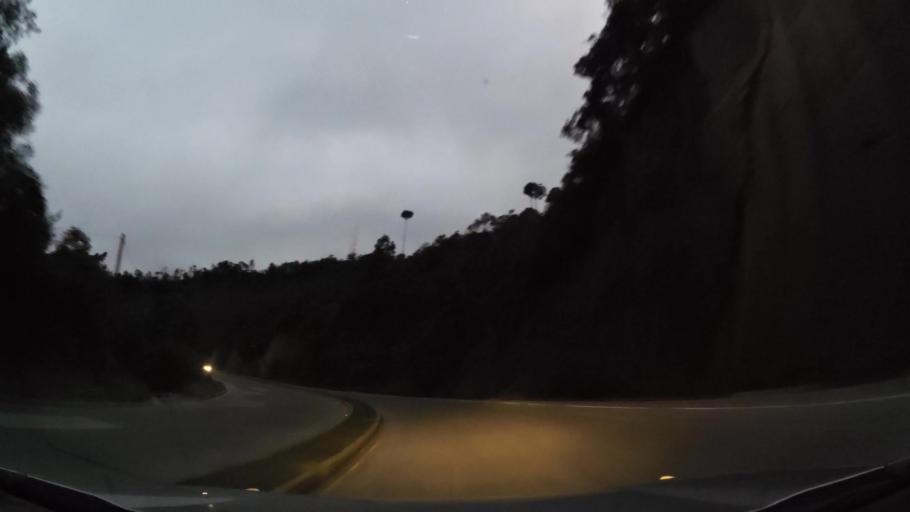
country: GT
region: Chimaltenango
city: Santa Apolonia
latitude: 14.8201
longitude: -91.0058
